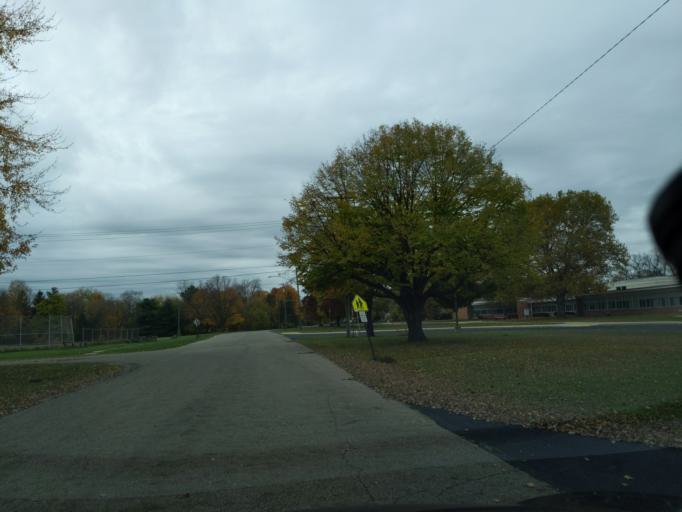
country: US
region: Michigan
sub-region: Eaton County
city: Eaton Rapids
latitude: 42.5153
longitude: -84.6455
